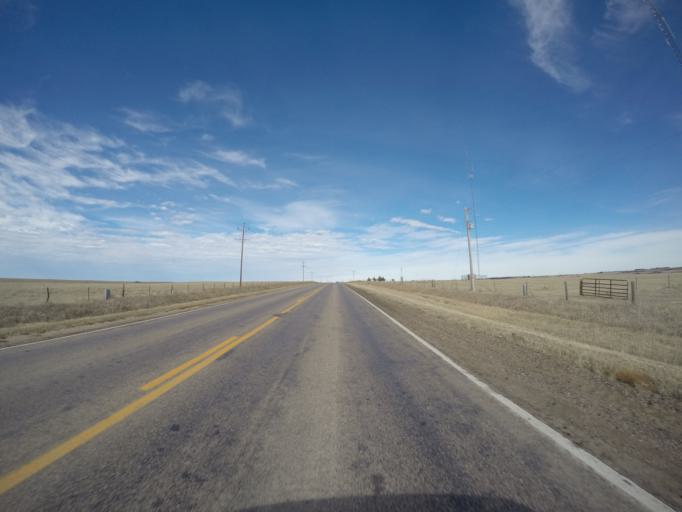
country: US
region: Nebraska
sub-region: Franklin County
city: Franklin
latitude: 40.1362
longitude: -98.9523
